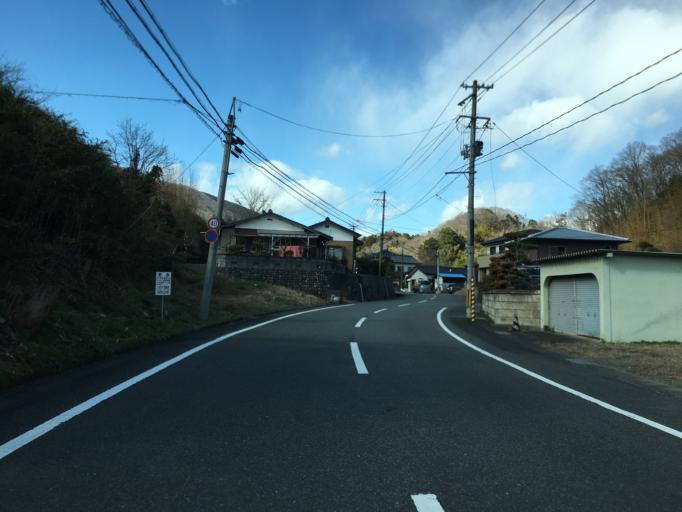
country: JP
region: Fukushima
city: Iwaki
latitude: 37.0115
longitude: 140.8253
